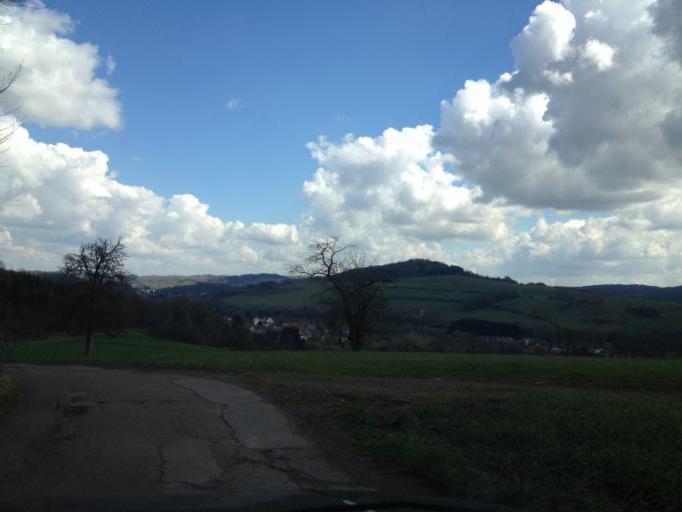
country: DE
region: Rheinland-Pfalz
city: Breitenbach
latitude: 49.4458
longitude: 7.2207
